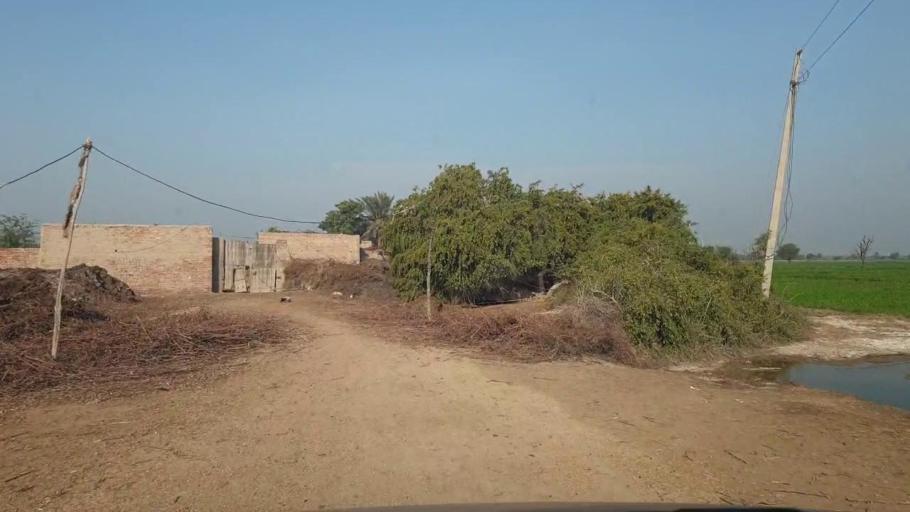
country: PK
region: Sindh
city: Tando Adam
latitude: 25.7334
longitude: 68.6060
